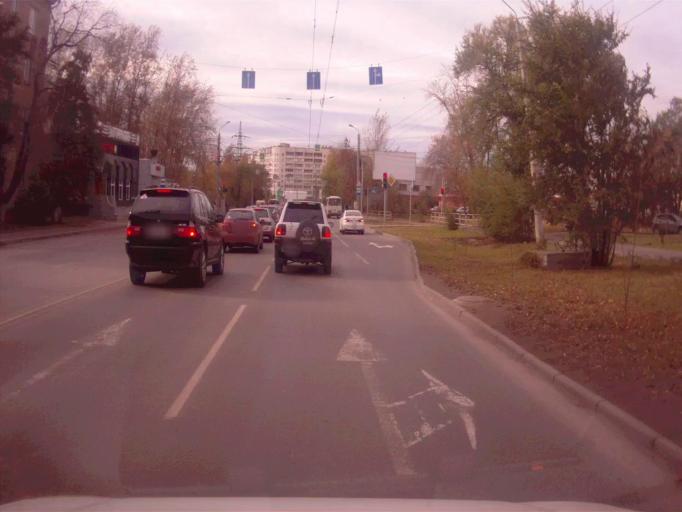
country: RU
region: Chelyabinsk
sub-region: Gorod Chelyabinsk
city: Chelyabinsk
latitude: 55.1159
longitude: 61.4466
